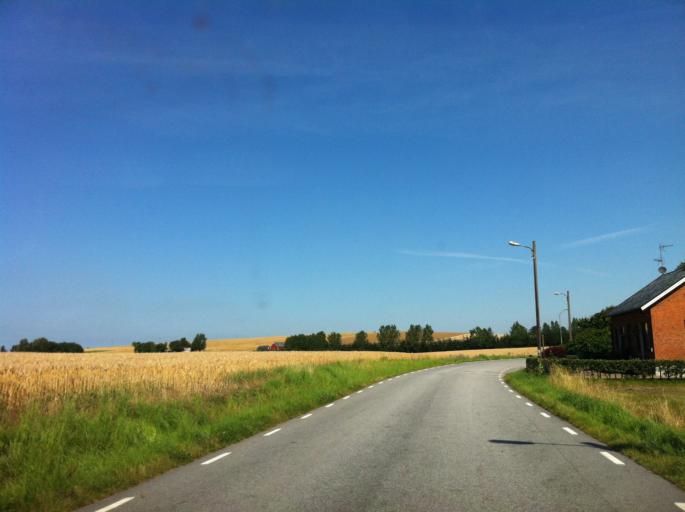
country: SE
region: Skane
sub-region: Landskrona
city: Asmundtorp
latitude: 55.9045
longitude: 12.9004
